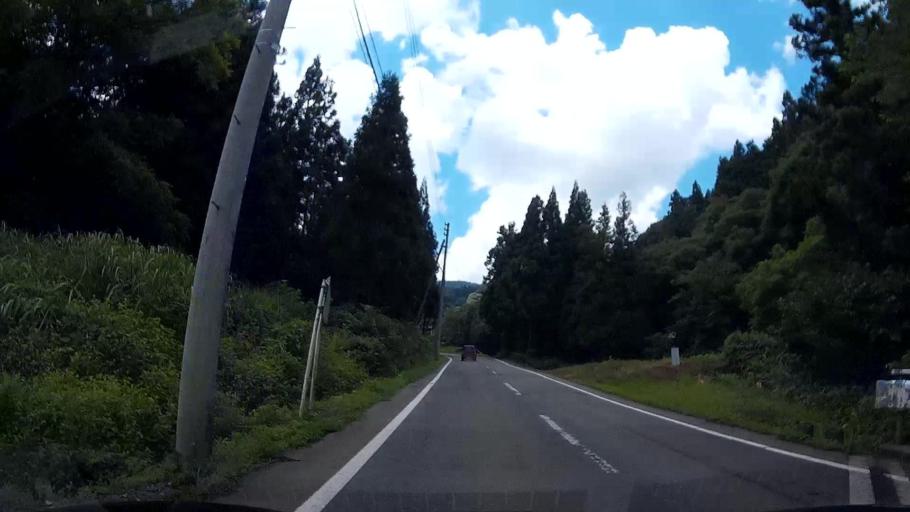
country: JP
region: Niigata
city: Shiozawa
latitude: 37.0201
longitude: 138.8162
